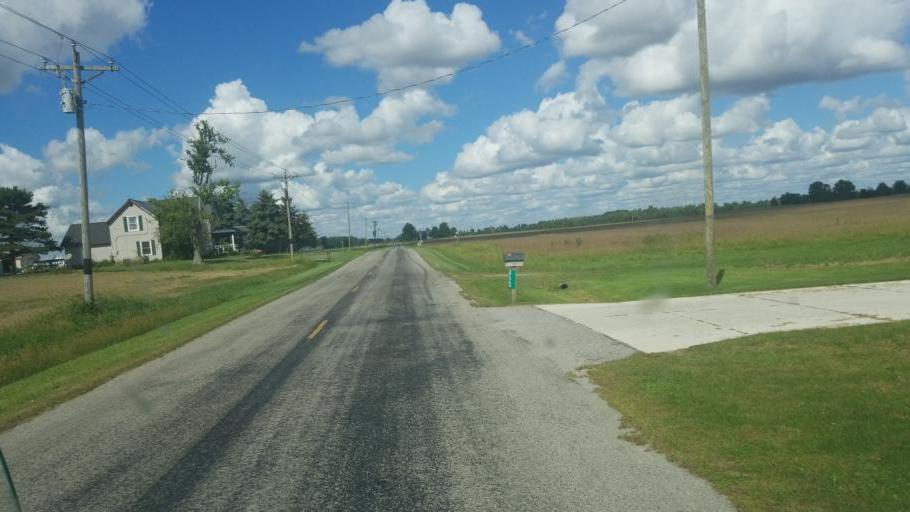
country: US
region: Ohio
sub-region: Champaign County
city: North Lewisburg
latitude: 40.3892
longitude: -83.5049
